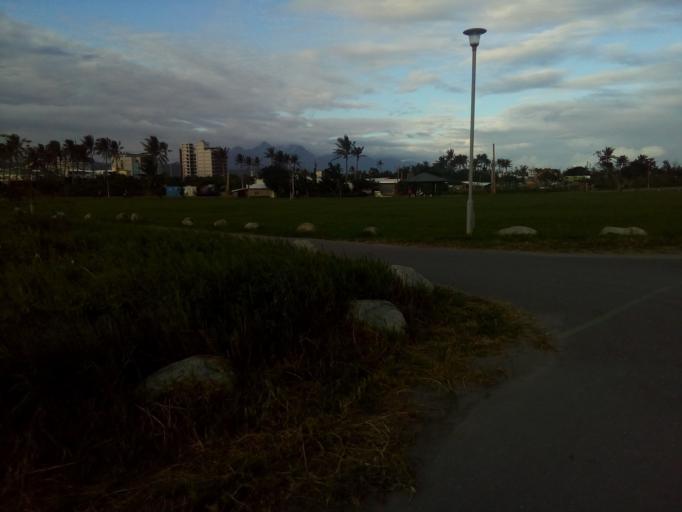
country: TW
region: Taiwan
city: Taitung City
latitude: 22.7512
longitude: 121.1615
